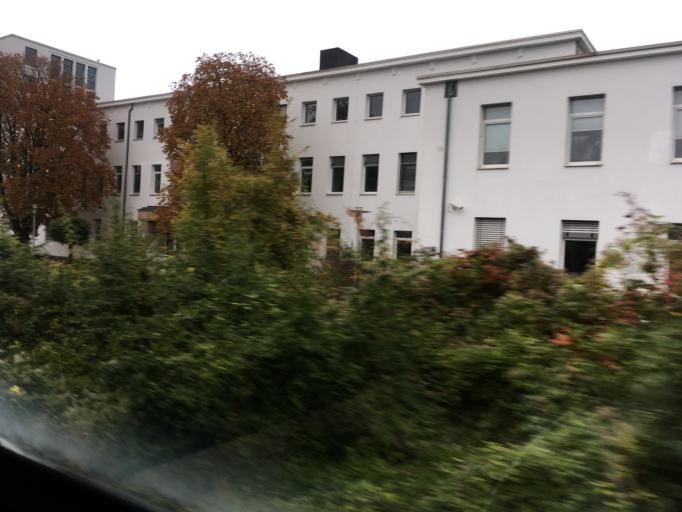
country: DE
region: Lower Saxony
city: Osnabrueck
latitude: 52.2719
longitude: 8.0647
